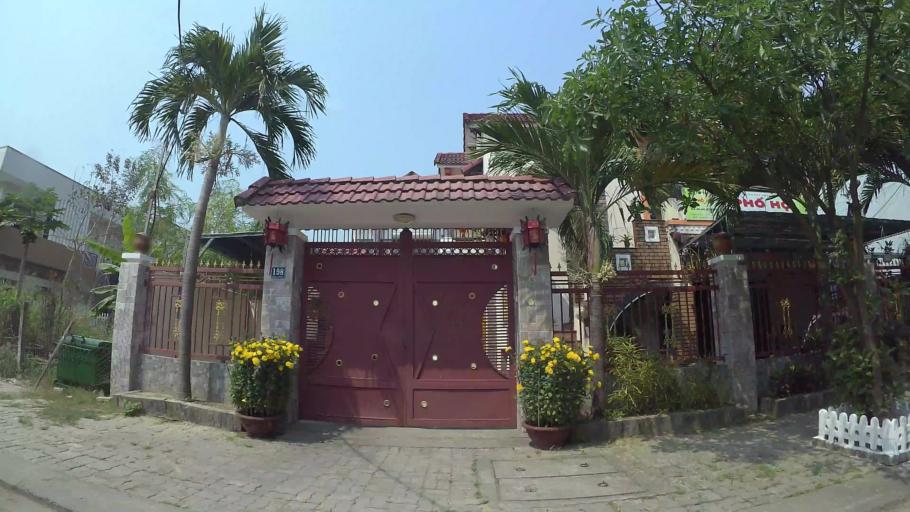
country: VN
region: Da Nang
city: Cam Le
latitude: 15.9856
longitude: 108.2089
